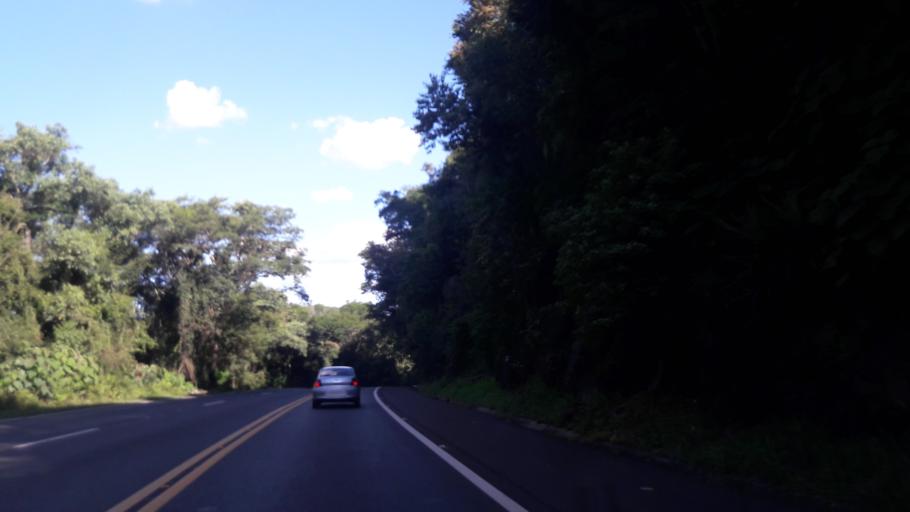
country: BR
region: Parana
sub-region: Laranjeiras Do Sul
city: Laranjeiras do Sul
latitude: -25.4158
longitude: -52.0729
